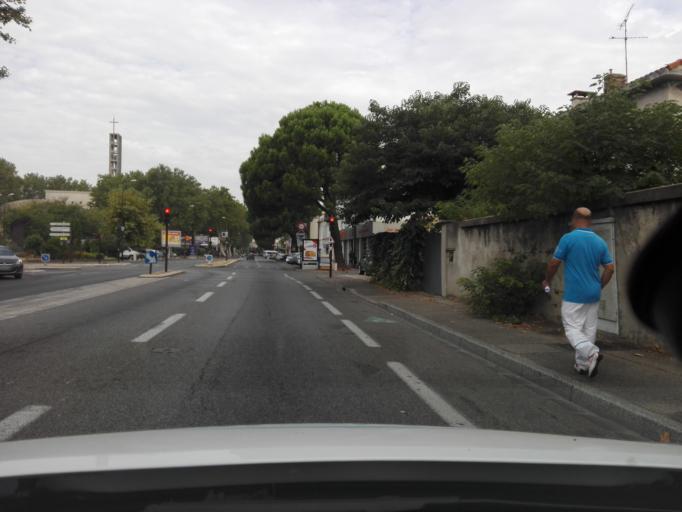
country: FR
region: Provence-Alpes-Cote d'Azur
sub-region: Departement du Vaucluse
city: Avignon
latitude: 43.9392
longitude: 4.8217
